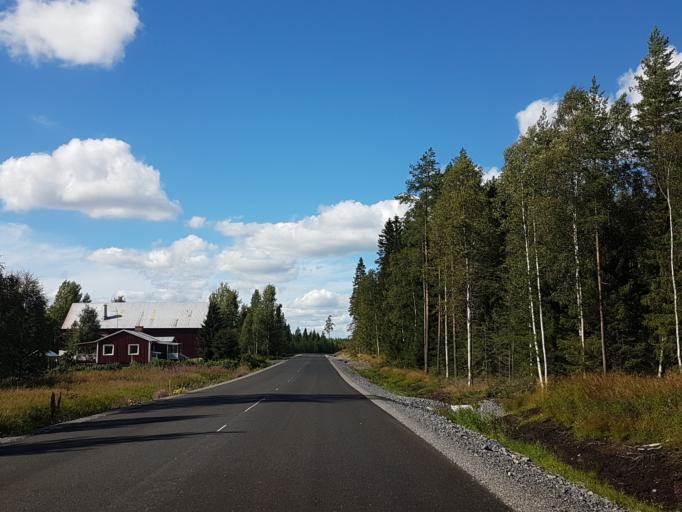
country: SE
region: Vaesterbotten
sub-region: Robertsfors Kommun
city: Robertsfors
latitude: 64.1313
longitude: 20.6401
